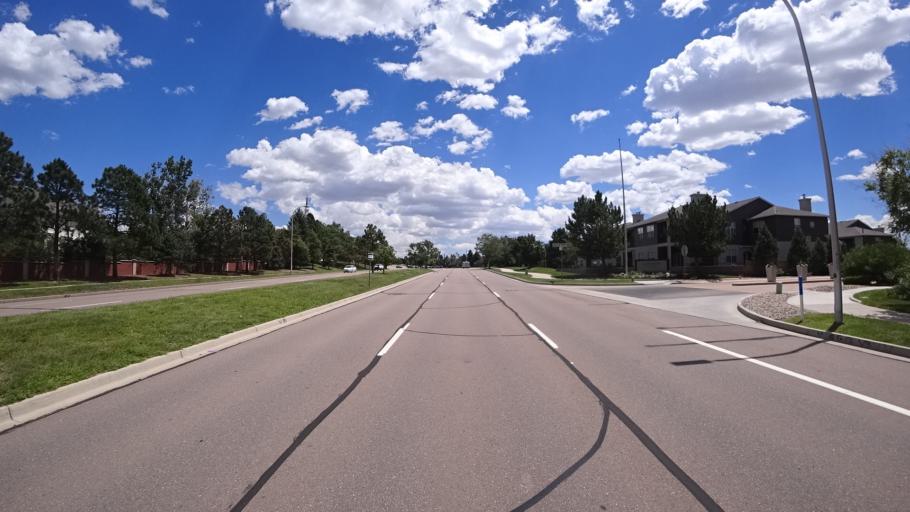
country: US
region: Colorado
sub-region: El Paso County
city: Black Forest
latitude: 38.9579
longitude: -104.7726
